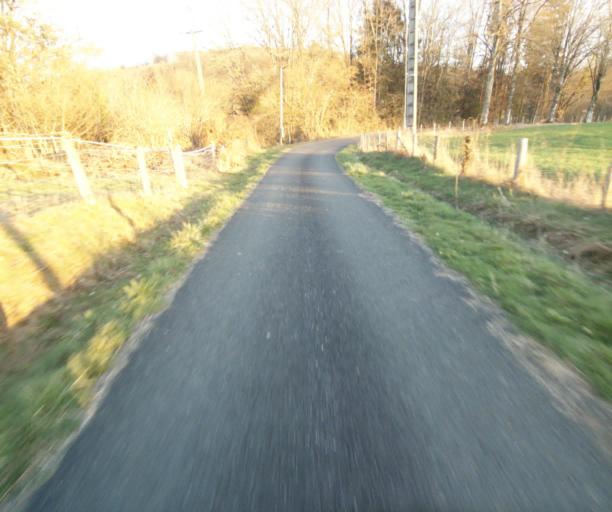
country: FR
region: Limousin
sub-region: Departement de la Correze
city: Uzerche
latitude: 45.3630
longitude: 1.6127
